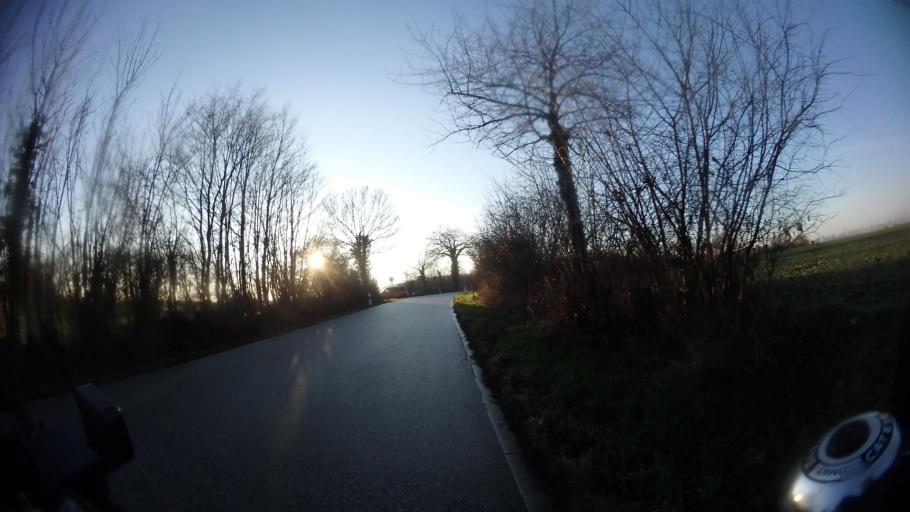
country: DE
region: Schleswig-Holstein
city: Travemuende
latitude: 53.9890
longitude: 10.8569
